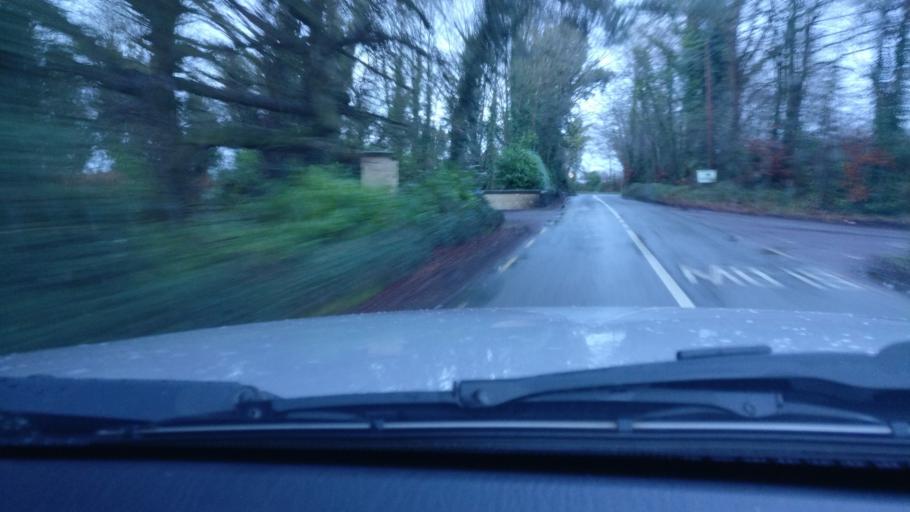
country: IE
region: Connaught
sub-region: County Galway
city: Ballinasloe
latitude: 53.2766
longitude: -8.2429
